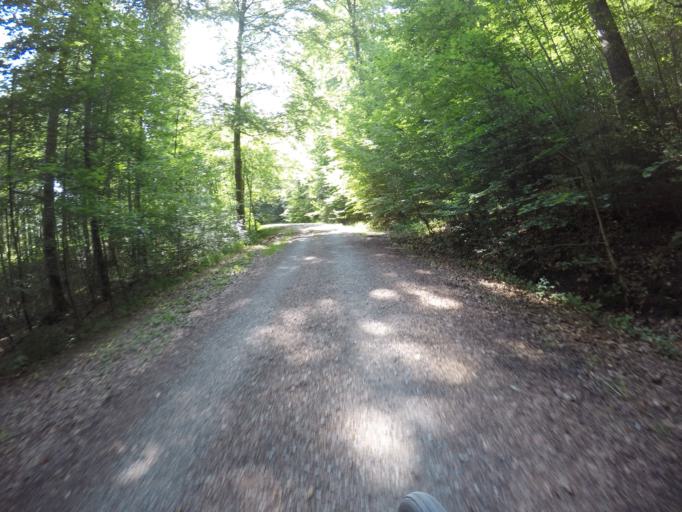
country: DE
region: Baden-Wuerttemberg
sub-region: Regierungsbezirk Stuttgart
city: Schlaitdorf
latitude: 48.6275
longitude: 9.1917
